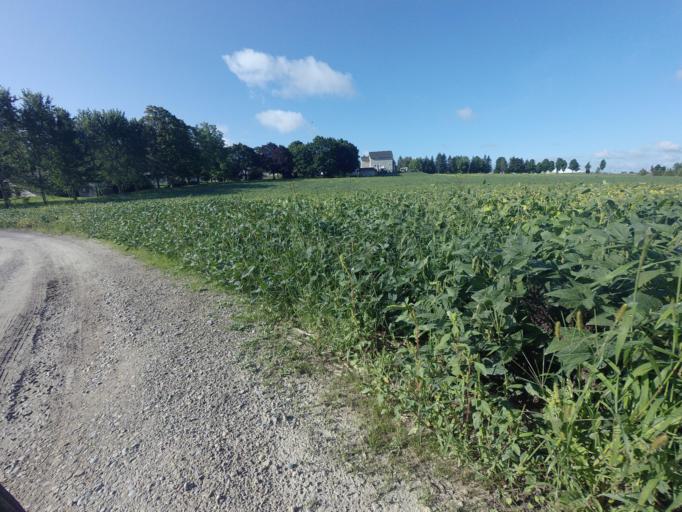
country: CA
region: Ontario
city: Huron East
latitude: 43.7389
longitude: -81.4312
